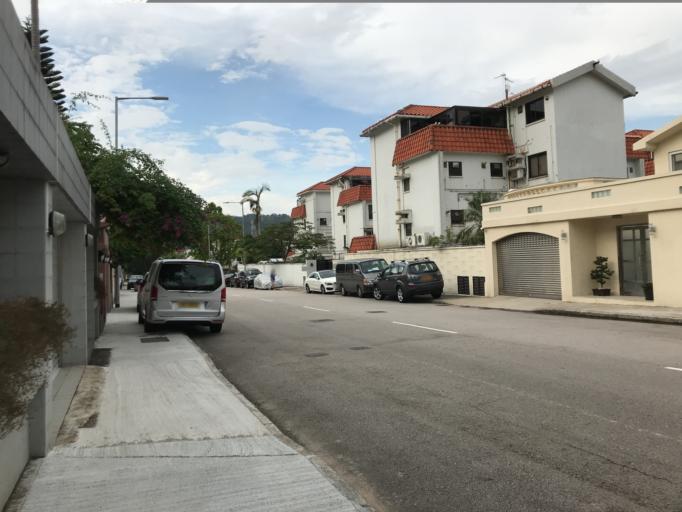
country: HK
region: Tai Po
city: Tai Po
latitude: 22.4620
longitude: 114.1555
